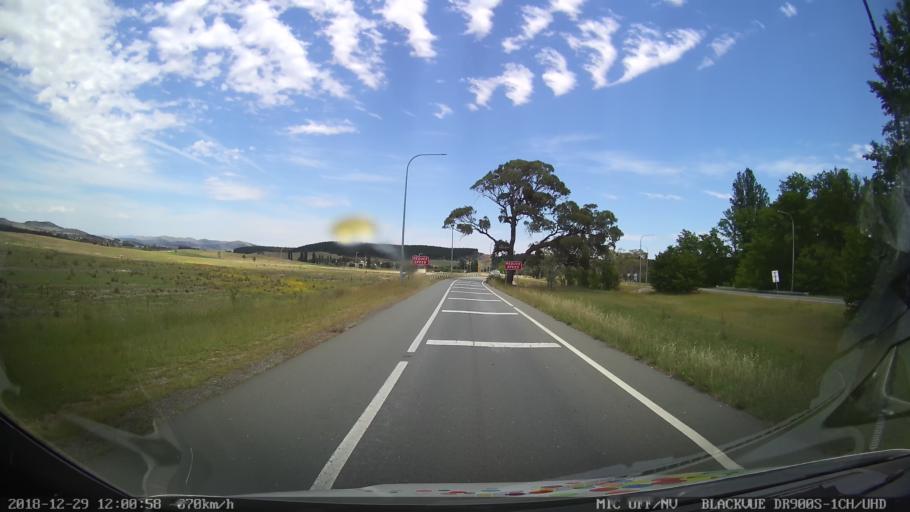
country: AU
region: New South Wales
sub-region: Palerang
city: Bungendore
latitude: -35.3213
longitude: 149.3838
